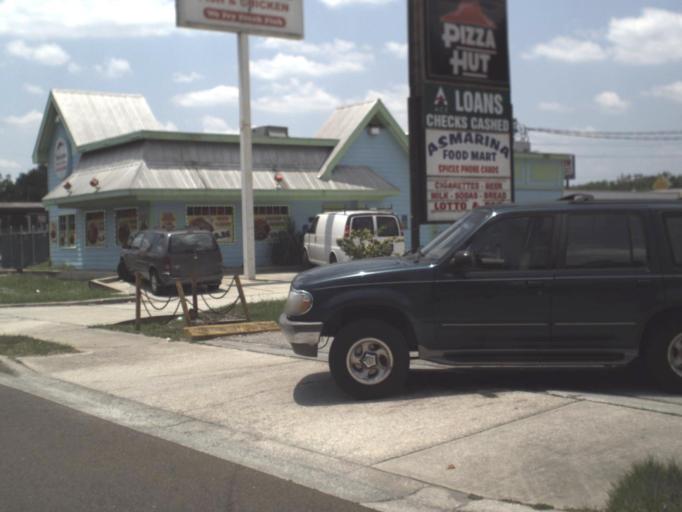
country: US
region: Florida
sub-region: Duval County
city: Jacksonville
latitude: 30.3102
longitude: -81.7307
